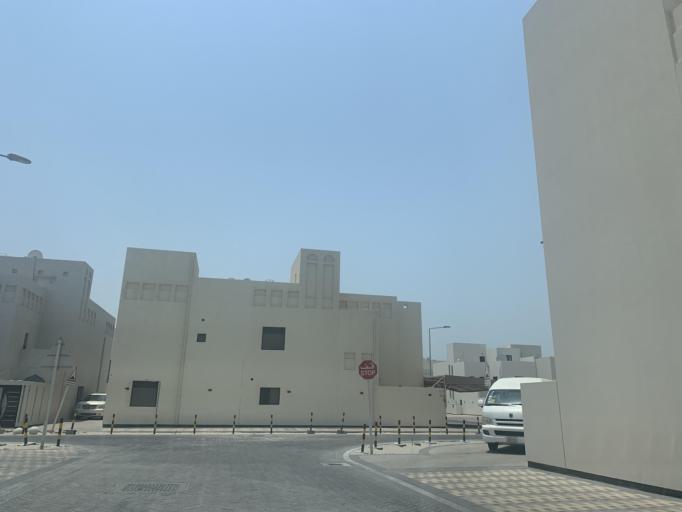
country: BH
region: Muharraq
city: Al Hadd
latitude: 26.2323
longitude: 50.6746
